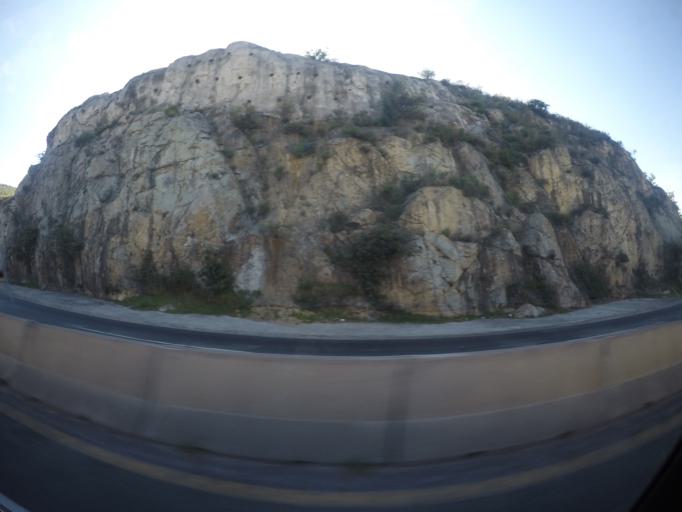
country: MX
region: Hidalgo
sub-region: Mineral de la Reforma
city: Colonia Militar
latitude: 20.1238
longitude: -98.6949
